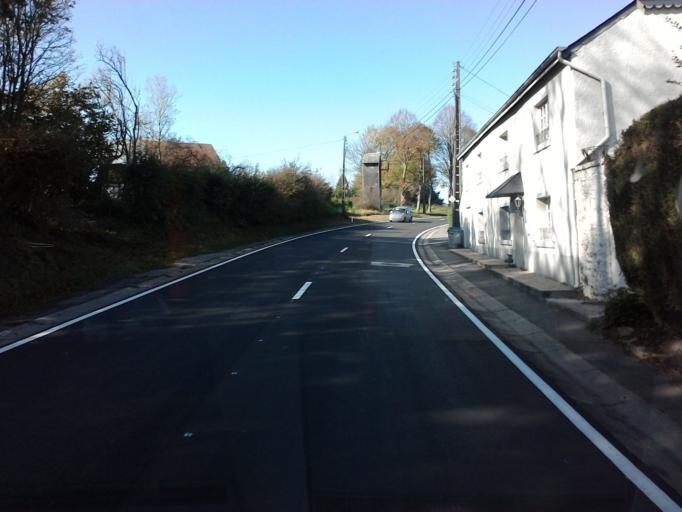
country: BE
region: Wallonia
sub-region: Province du Luxembourg
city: Florenville
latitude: 49.7168
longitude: 5.3163
